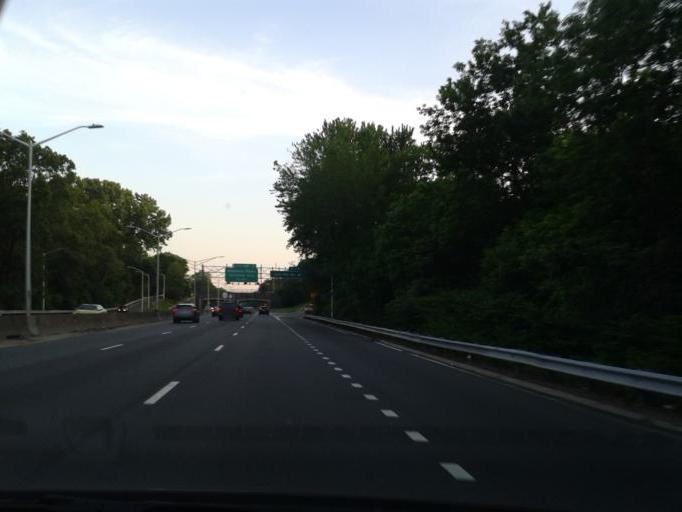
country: US
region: New York
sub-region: Bronx
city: The Bronx
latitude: 40.8809
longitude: -73.8693
